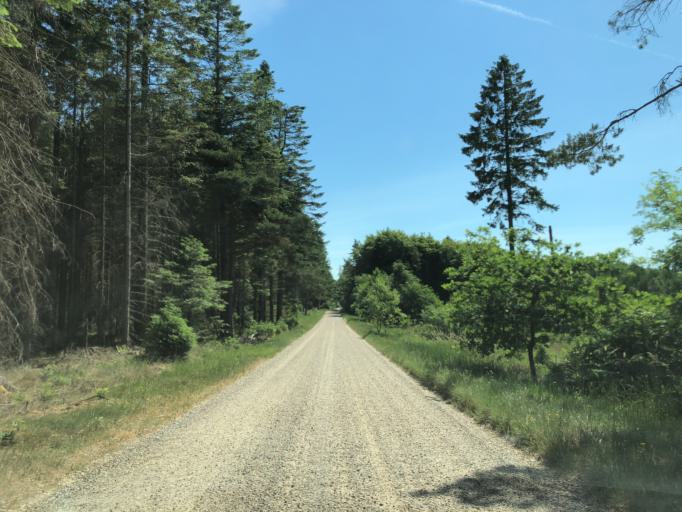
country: DK
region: Central Jutland
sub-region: Struer Kommune
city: Struer
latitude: 56.4370
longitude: 8.4436
